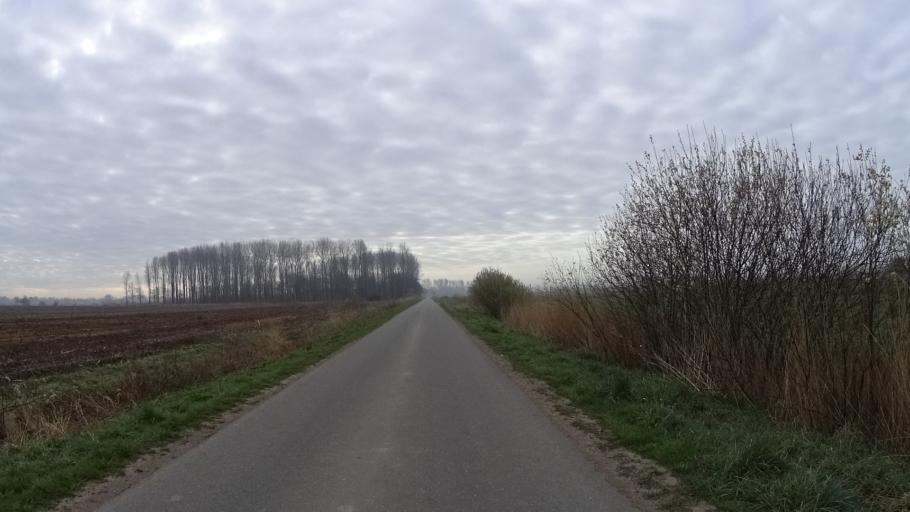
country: DE
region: Lower Saxony
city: Upgant-Schott
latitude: 53.4574
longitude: 7.3255
